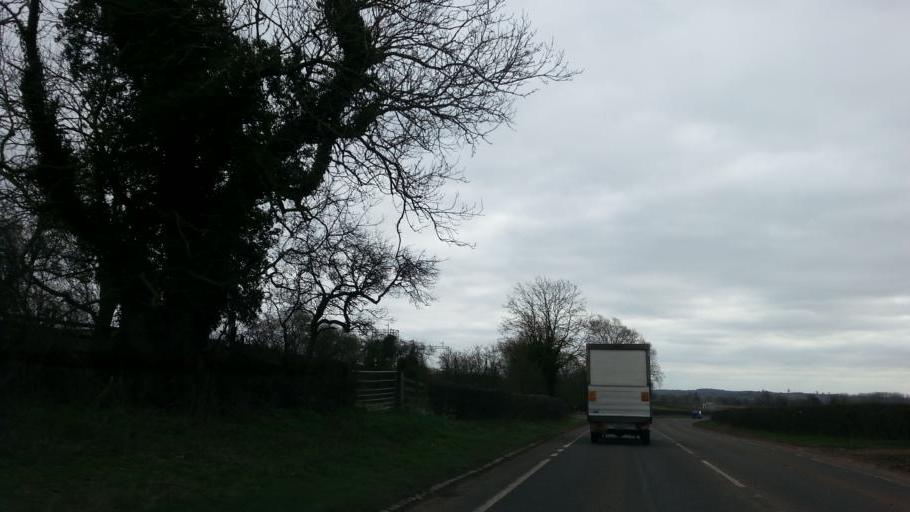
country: GB
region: England
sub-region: Staffordshire
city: Stone
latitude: 52.8837
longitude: -2.1174
